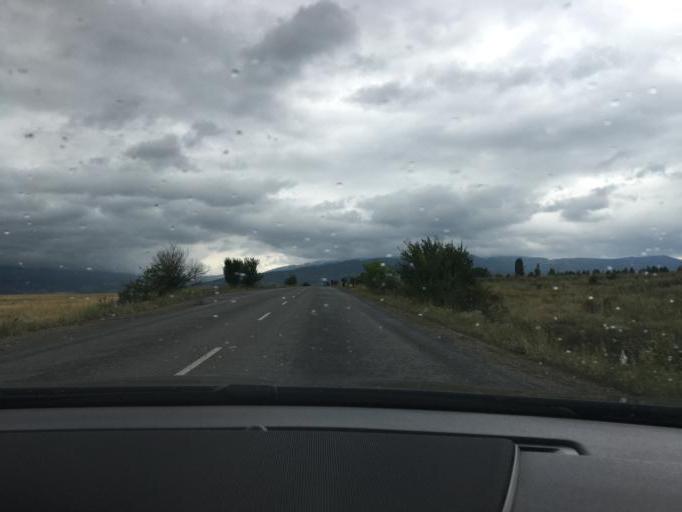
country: BG
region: Kyustendil
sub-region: Obshtina Kyustendil
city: Kyustendil
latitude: 42.3016
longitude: 22.7009
